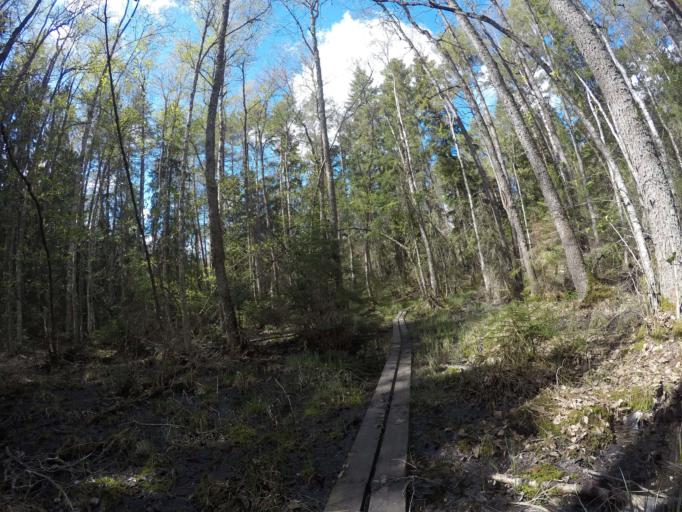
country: SE
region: Soedermanland
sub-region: Eskilstuna Kommun
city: Hallbybrunn
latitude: 59.3527
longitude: 16.4014
